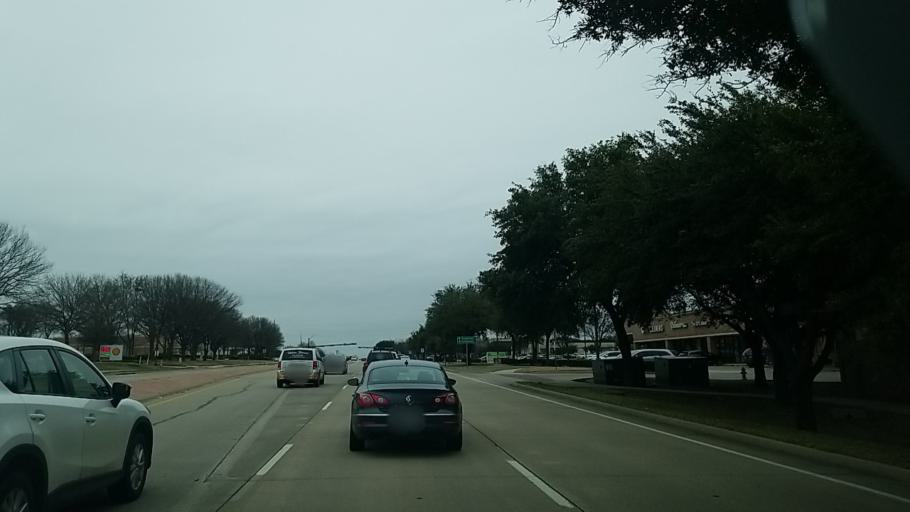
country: US
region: Texas
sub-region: Denton County
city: Flower Mound
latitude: 33.0167
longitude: -97.0708
